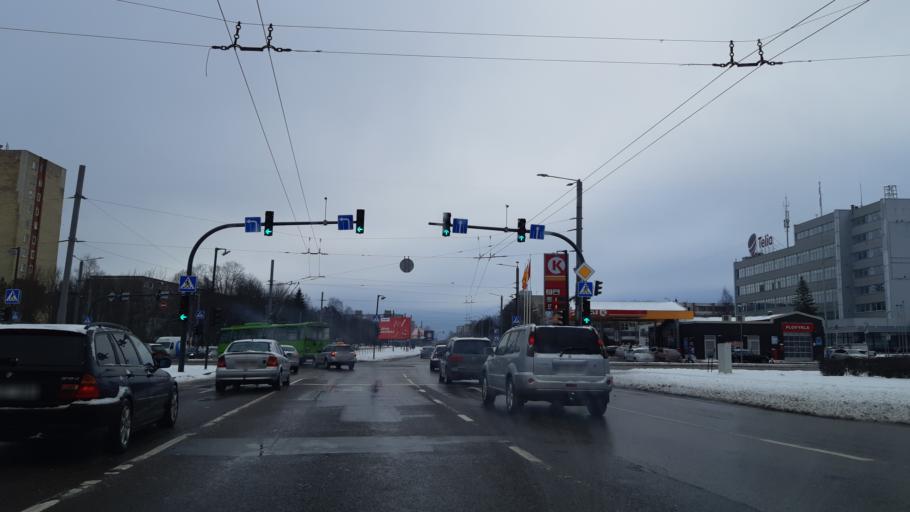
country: LT
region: Kauno apskritis
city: Dainava (Kaunas)
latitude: 54.9122
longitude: 23.9554
